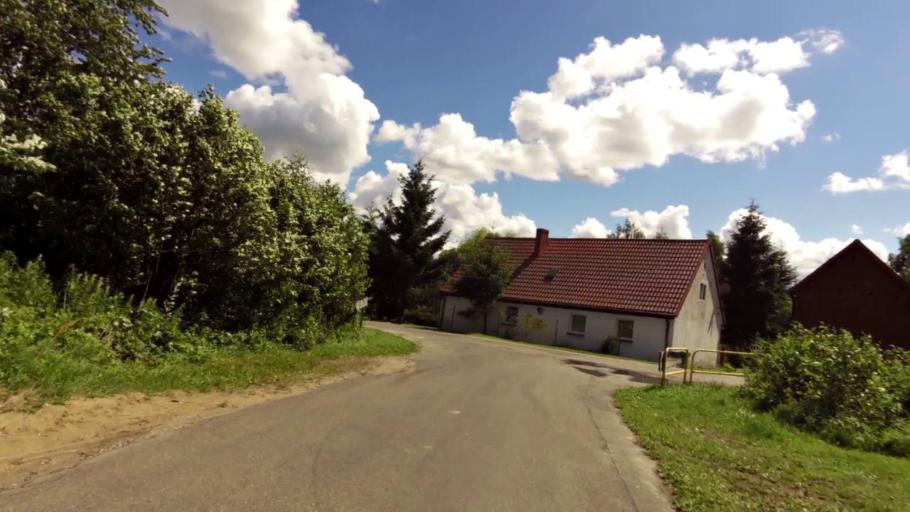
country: PL
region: West Pomeranian Voivodeship
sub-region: Powiat slawienski
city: Slawno
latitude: 54.5240
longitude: 16.6080
